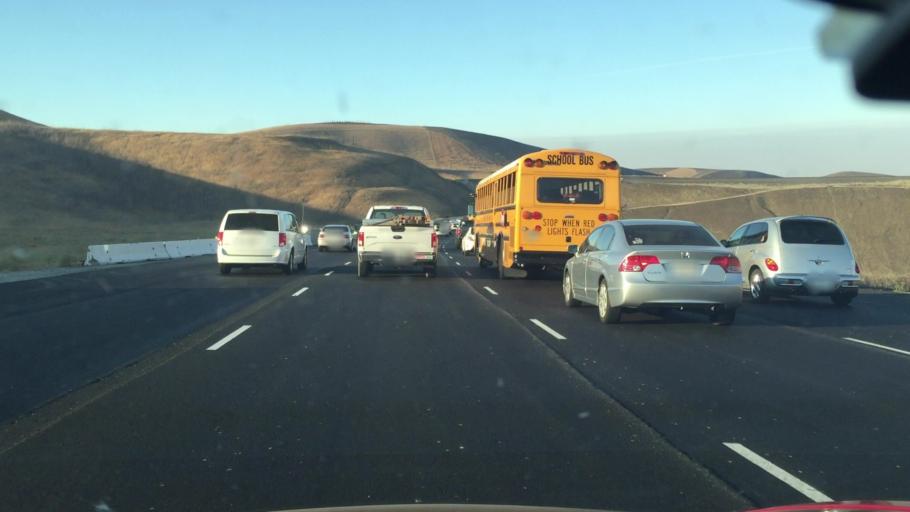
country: US
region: California
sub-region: San Joaquin County
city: Mountain House
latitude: 37.7303
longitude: -121.6326
